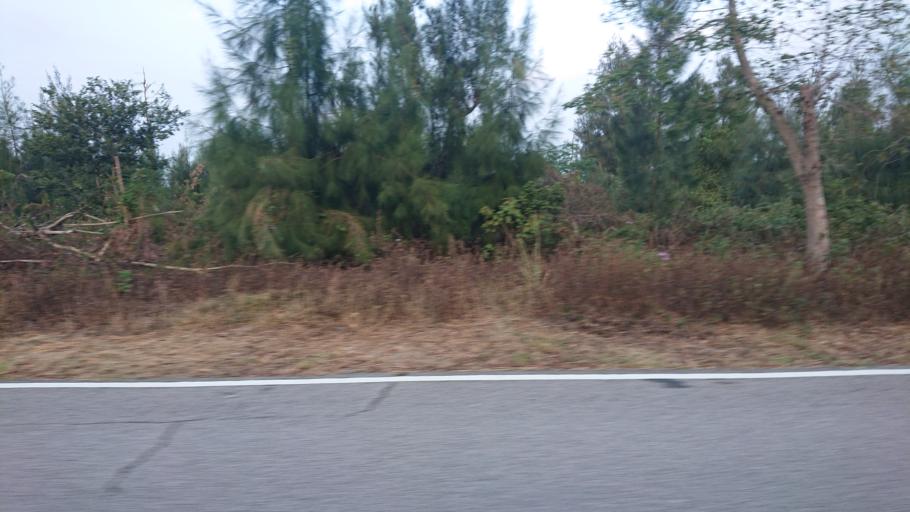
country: CN
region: Fujian
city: Shijing
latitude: 24.4961
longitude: 118.4440
